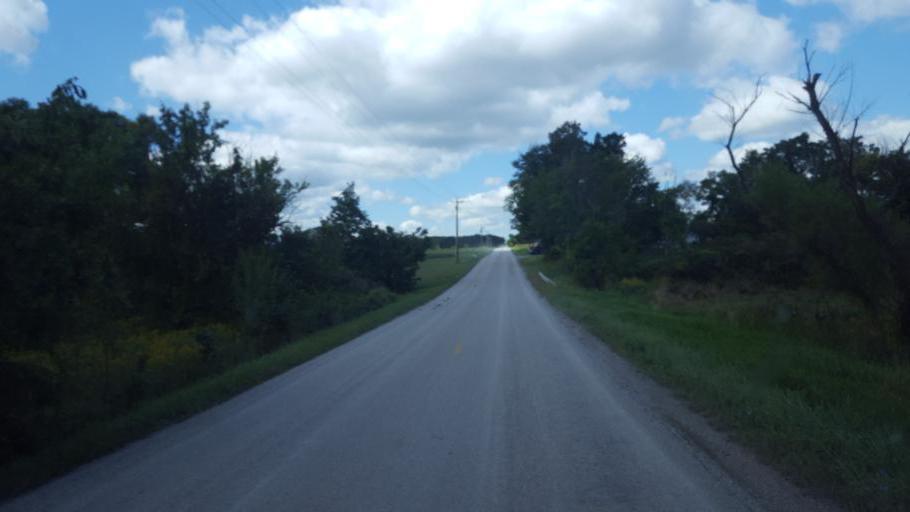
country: US
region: Ohio
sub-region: Wayne County
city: West Salem
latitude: 40.9920
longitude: -82.1573
